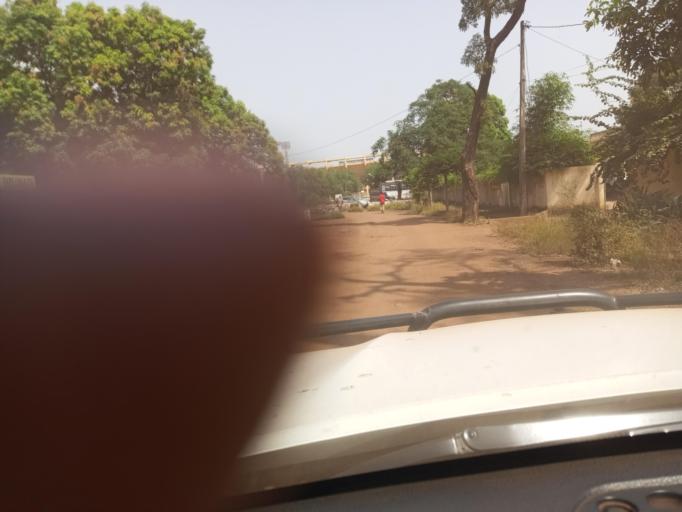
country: ML
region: Bamako
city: Bamako
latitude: 12.6597
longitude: -7.9963
